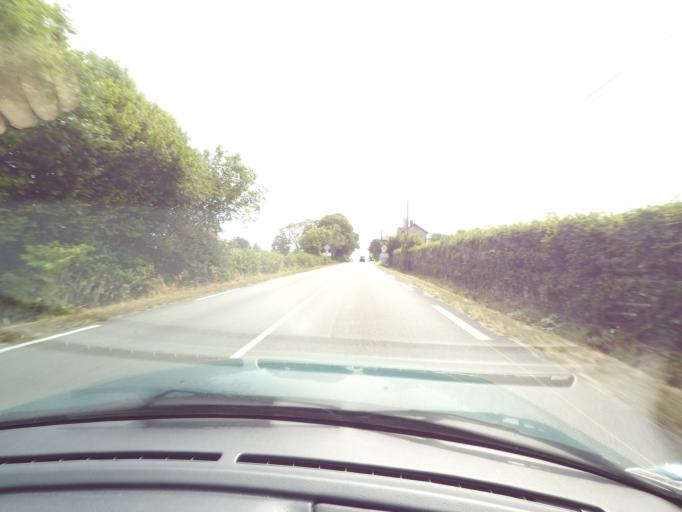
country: FR
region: Limousin
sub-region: Departement de la Haute-Vienne
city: Saint-Paul
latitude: 45.7974
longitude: 1.4206
